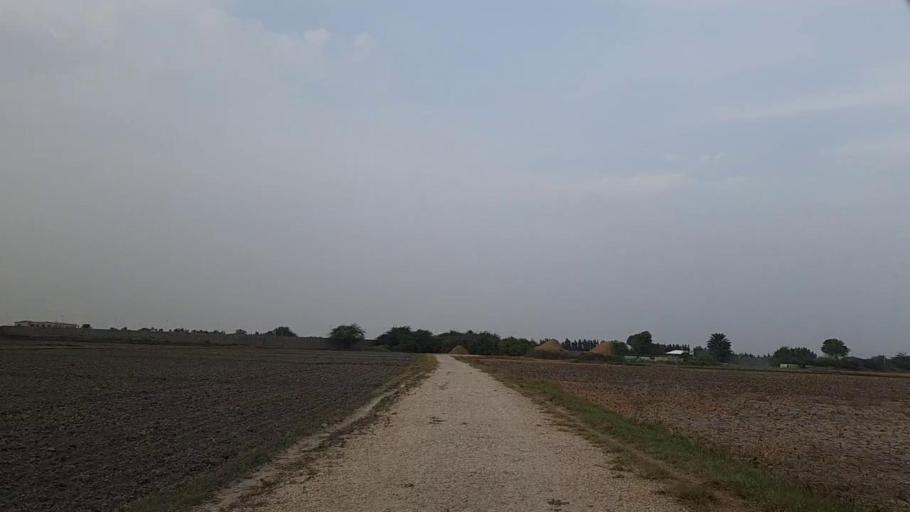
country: PK
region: Sindh
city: Thatta
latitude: 24.7473
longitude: 67.9374
